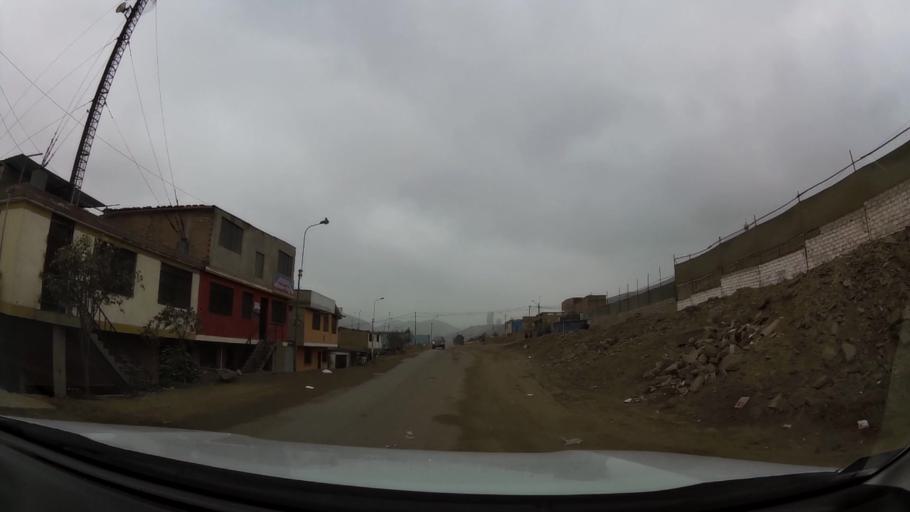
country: PE
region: Lima
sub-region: Lima
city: Cieneguilla
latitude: -12.2158
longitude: -76.9021
